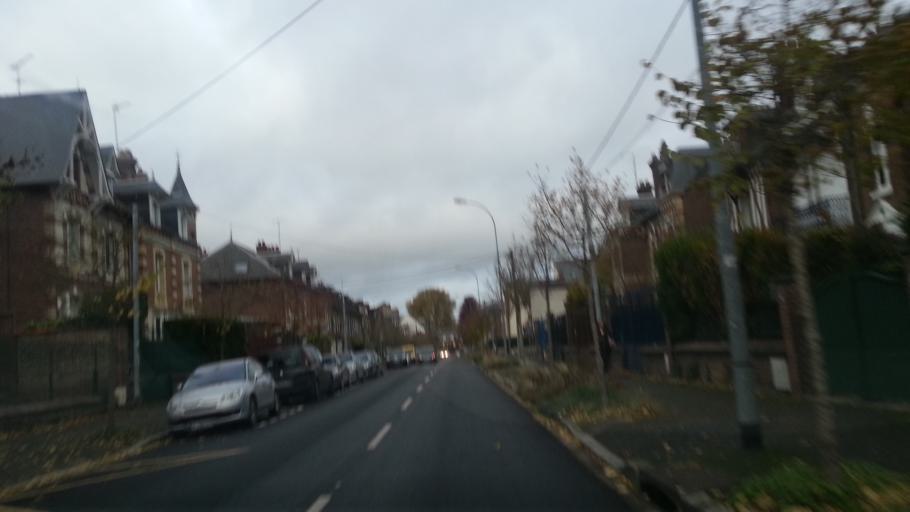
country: FR
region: Picardie
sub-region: Departement de l'Oise
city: Beauvais
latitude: 49.4350
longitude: 2.0783
